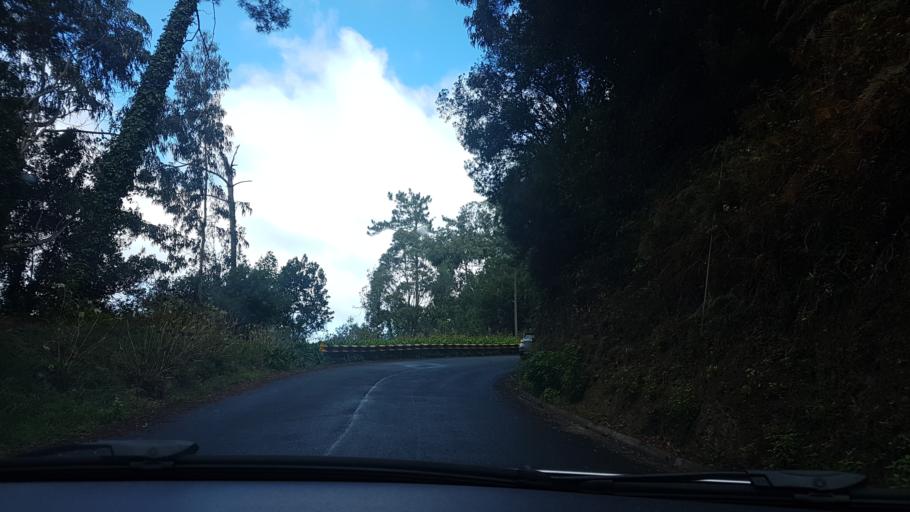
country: PT
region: Madeira
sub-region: Sao Vicente
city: Sao Vicente
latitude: 32.7649
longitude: -17.0285
